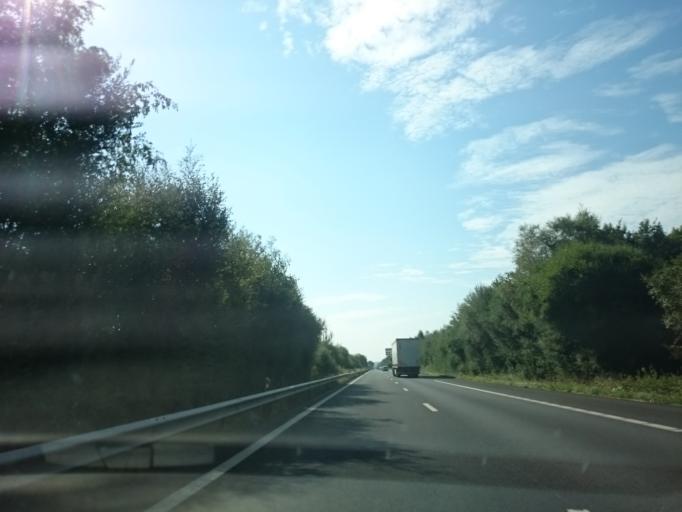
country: FR
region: Pays de la Loire
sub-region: Departement de la Loire-Atlantique
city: Jans
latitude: 47.6312
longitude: -1.6477
